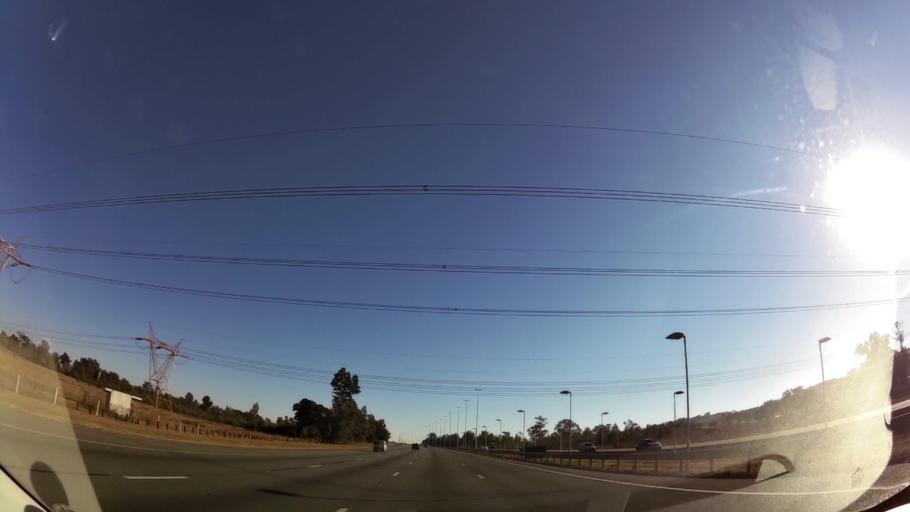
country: ZA
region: Gauteng
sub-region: Ekurhuleni Metropolitan Municipality
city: Tembisa
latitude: -25.9178
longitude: 28.2605
